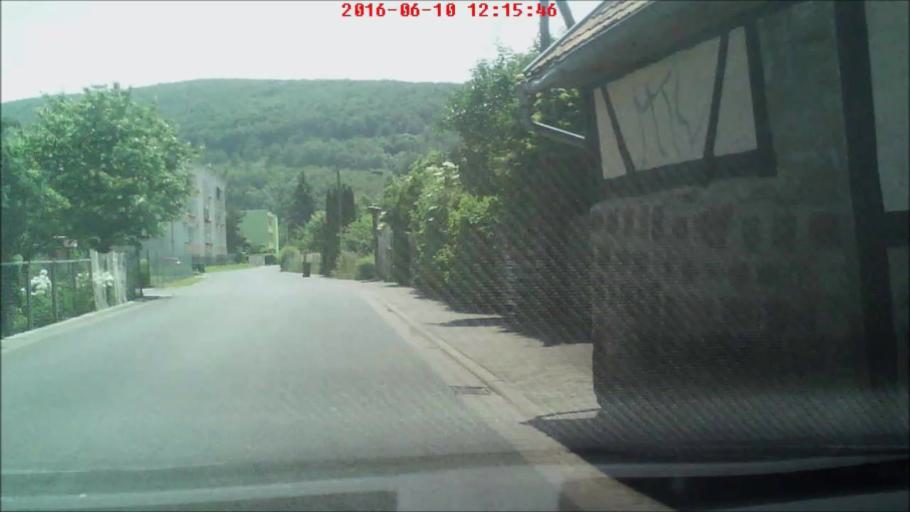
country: DE
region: Thuringia
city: Obermassfeld-Grimmenthal
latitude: 50.5292
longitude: 10.4412
